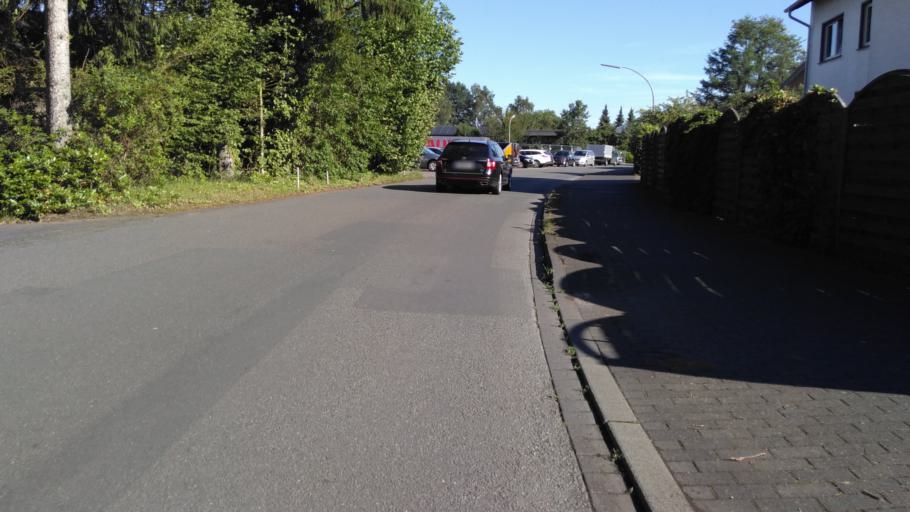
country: DE
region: North Rhine-Westphalia
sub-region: Regierungsbezirk Detmold
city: Verl
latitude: 51.8734
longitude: 8.4658
